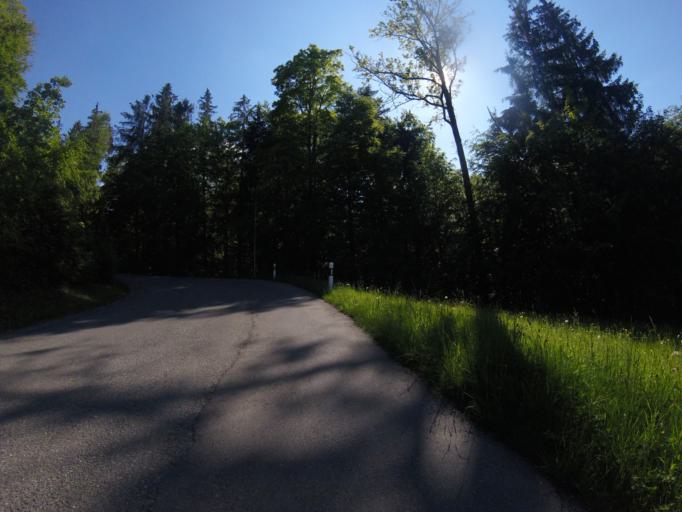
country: CH
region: Saint Gallen
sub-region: Wahlkreis Wil
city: Degersheim
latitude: 47.4007
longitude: 9.2162
